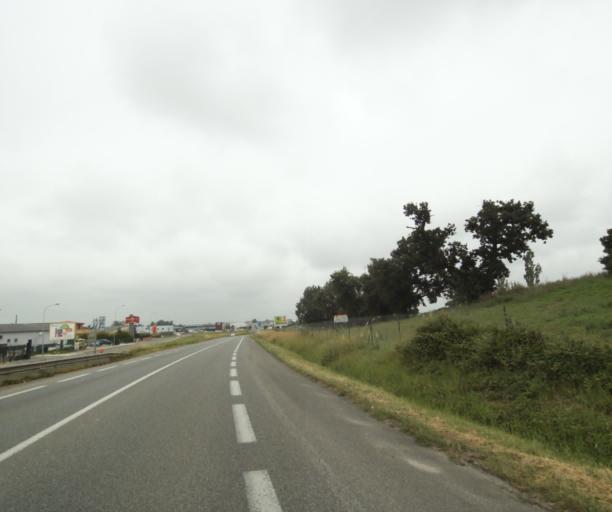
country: FR
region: Midi-Pyrenees
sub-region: Departement du Tarn-et-Garonne
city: Bressols
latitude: 43.9799
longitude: 1.3314
